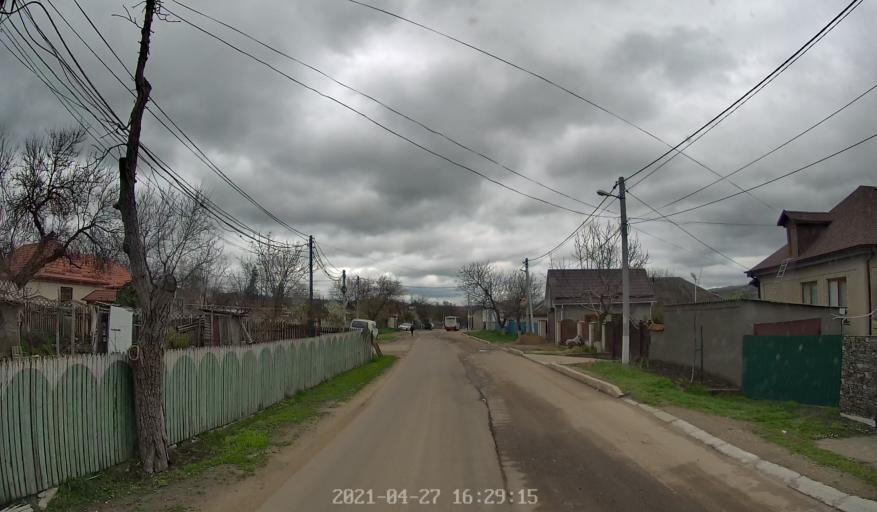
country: MD
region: Chisinau
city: Singera
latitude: 46.9683
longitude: 29.0494
